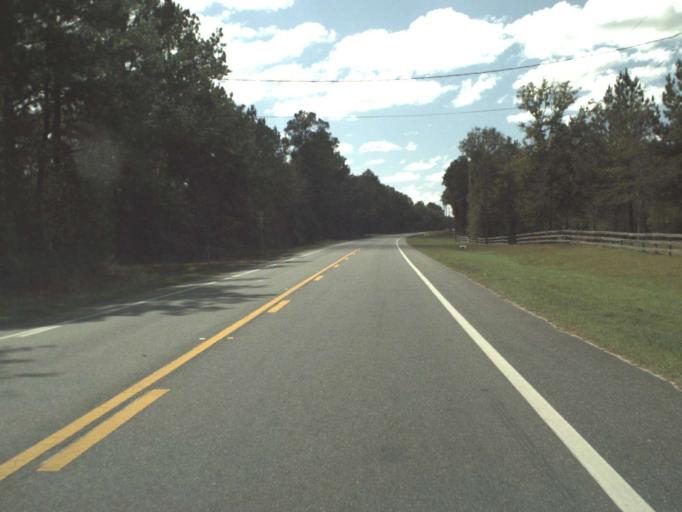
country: US
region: Florida
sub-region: Holmes County
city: Bonifay
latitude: 30.6900
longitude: -85.6297
